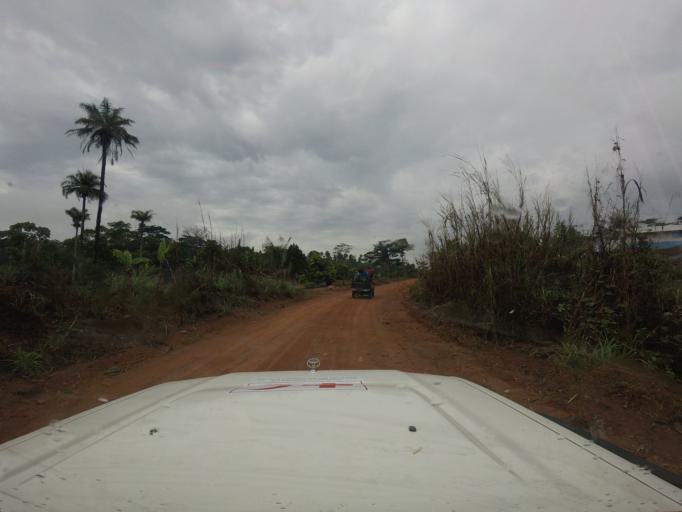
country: SL
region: Eastern Province
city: Buedu
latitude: 8.3154
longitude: -10.1502
